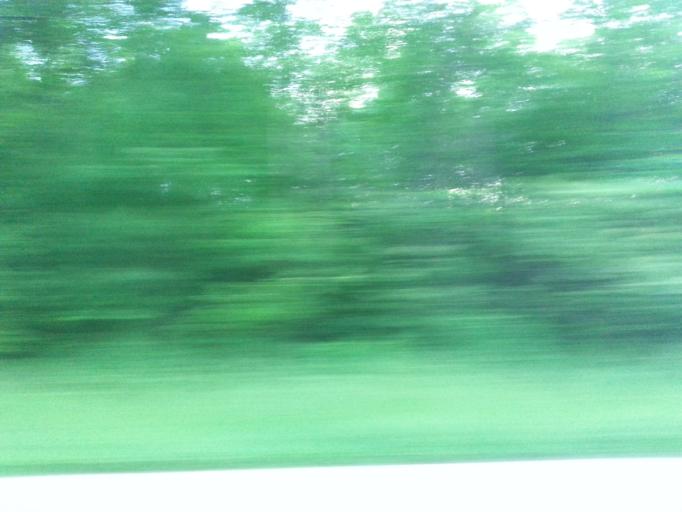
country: US
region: Tennessee
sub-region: Monroe County
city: Madisonville
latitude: 35.3137
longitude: -84.2941
